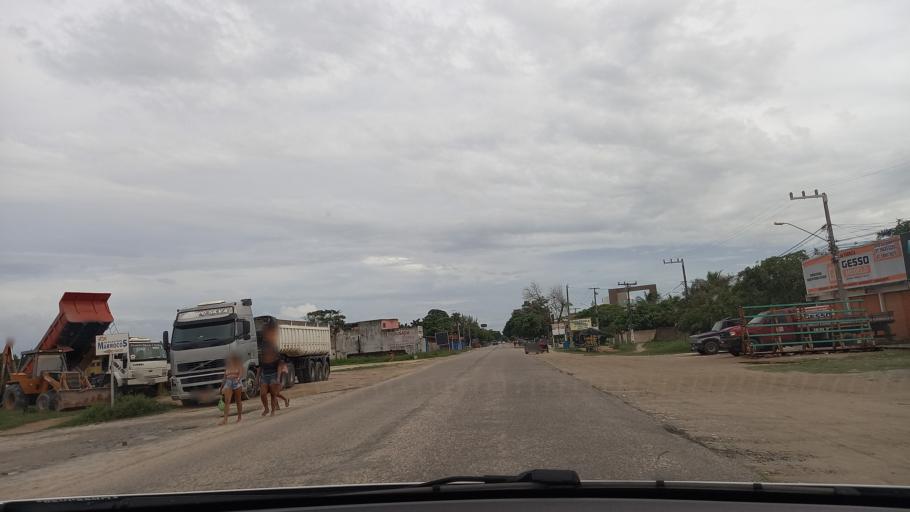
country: BR
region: Pernambuco
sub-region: Sao Jose Da Coroa Grande
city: Sao Jose da Coroa Grande
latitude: -8.8974
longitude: -35.1507
